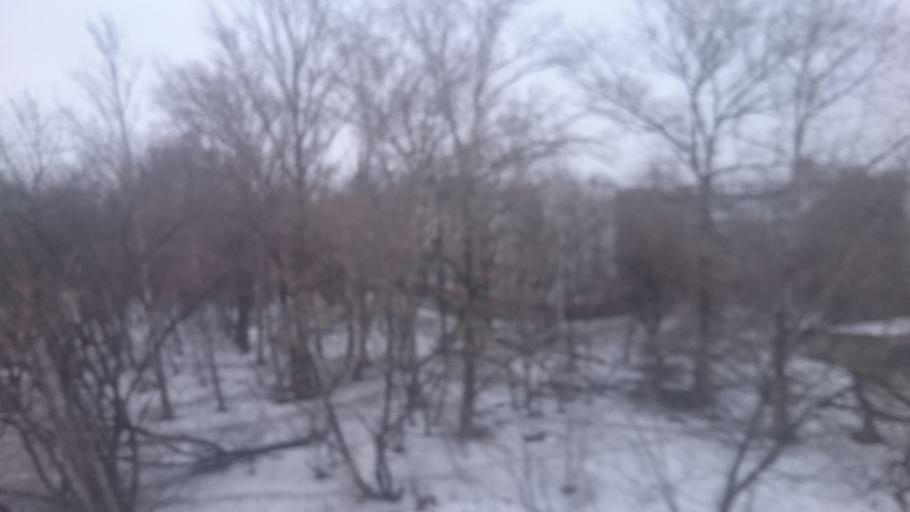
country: RU
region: Moscow
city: Pokrovskoye-Streshnevo
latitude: 55.8131
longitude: 37.4503
